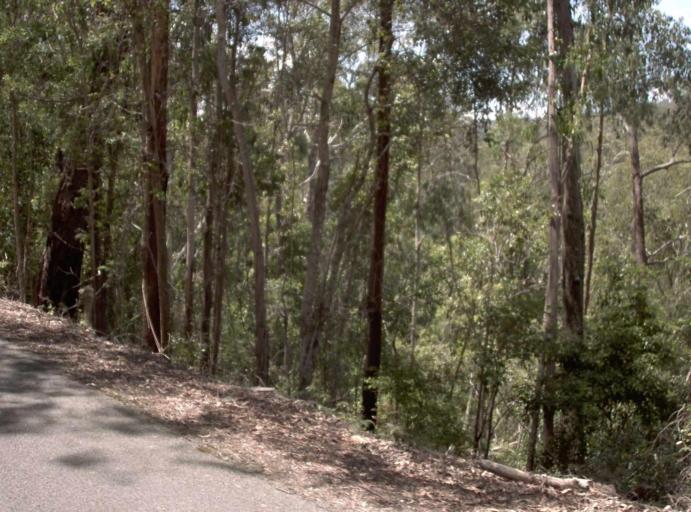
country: AU
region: New South Wales
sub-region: Bombala
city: Bombala
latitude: -37.5024
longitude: 148.9251
